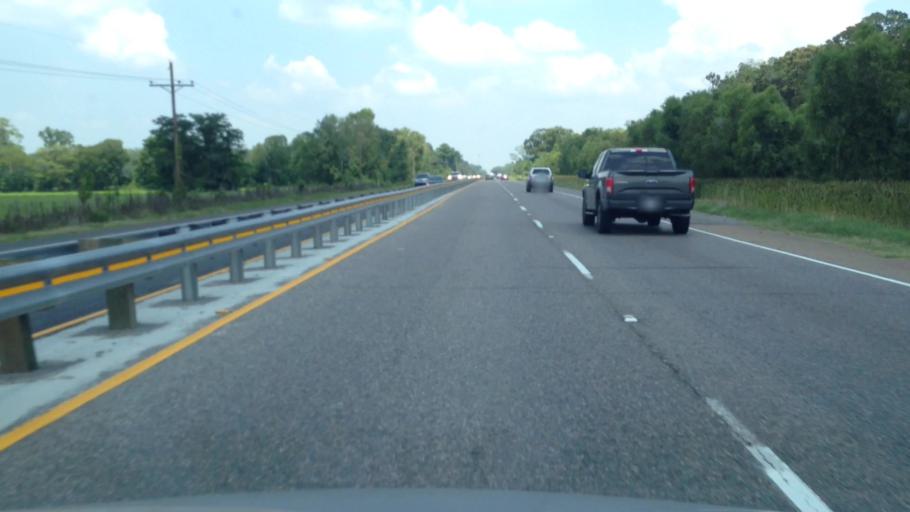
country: US
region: Louisiana
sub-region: Pointe Coupee Parish
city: Livonia
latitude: 30.5560
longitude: -91.6118
